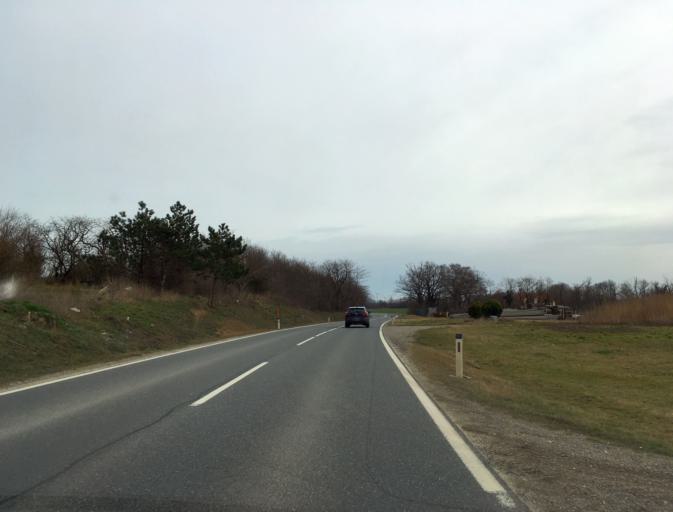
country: AT
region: Lower Austria
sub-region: Politischer Bezirk Ganserndorf
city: Parbasdorf
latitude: 48.2815
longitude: 16.5923
